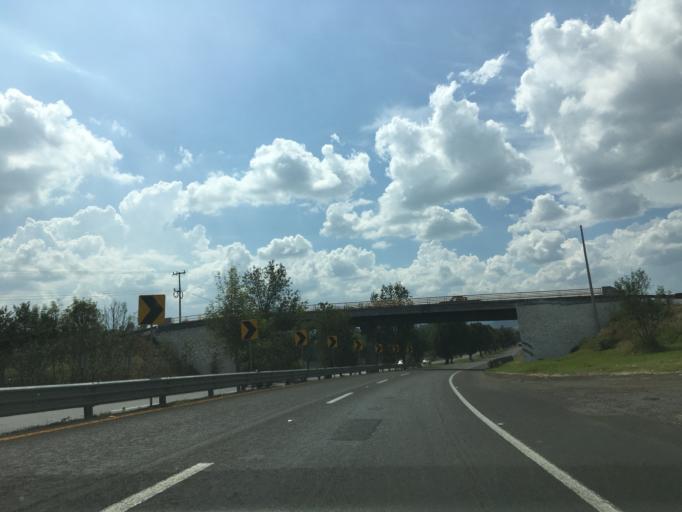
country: MX
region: Michoacan
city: Huiramba
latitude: 19.5501
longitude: -101.4321
